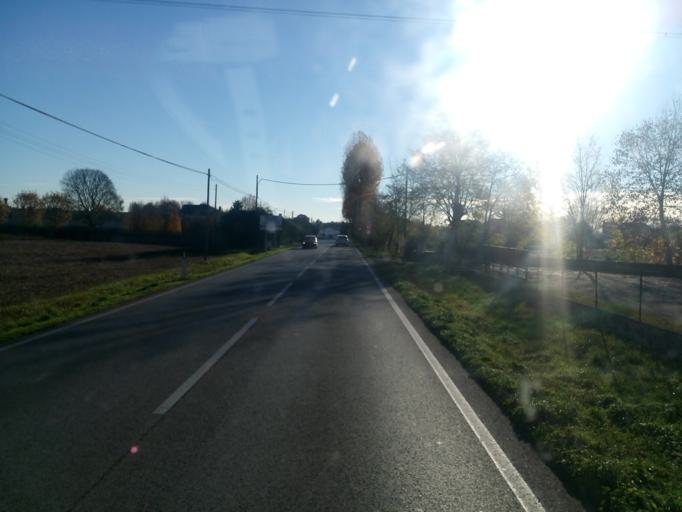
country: IT
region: Veneto
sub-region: Provincia di Padova
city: Galliera Veneta
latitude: 45.6938
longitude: 11.8416
